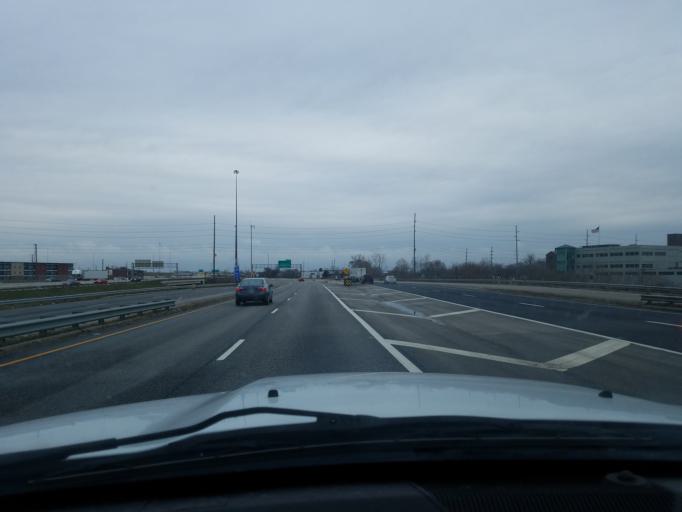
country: US
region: Indiana
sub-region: Marion County
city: Indianapolis
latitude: 39.7756
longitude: -86.1418
